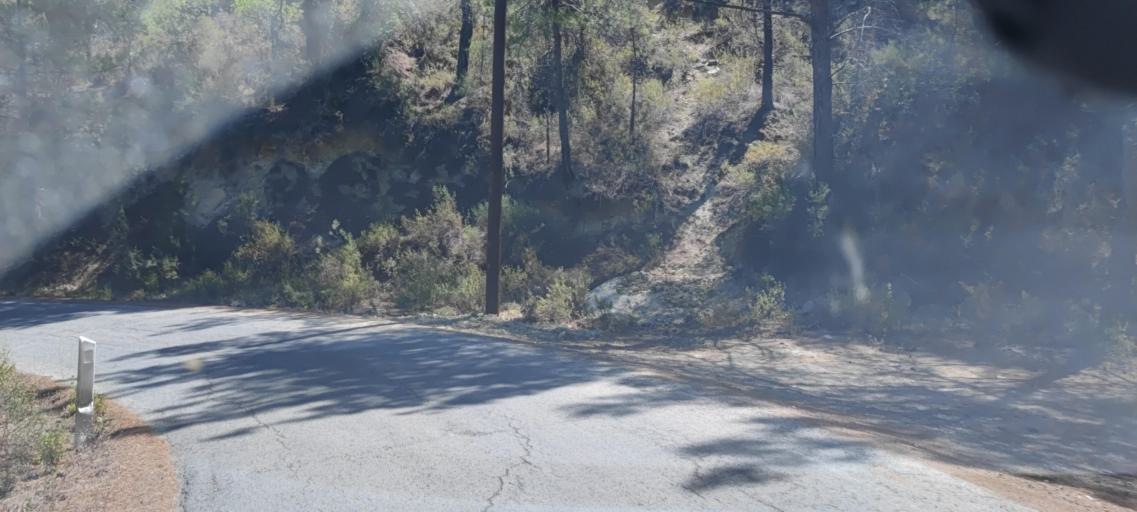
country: CY
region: Lefkosia
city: Kakopetria
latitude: 34.9229
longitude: 32.8111
